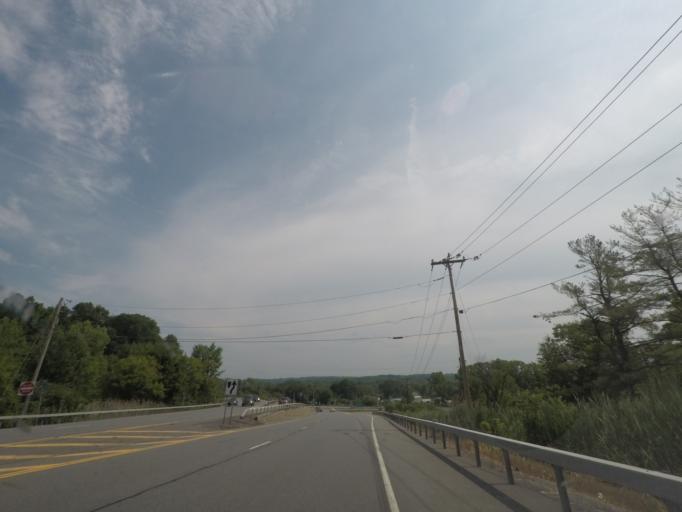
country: US
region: New York
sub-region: Saratoga County
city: Mechanicville
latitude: 42.8873
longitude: -73.6917
